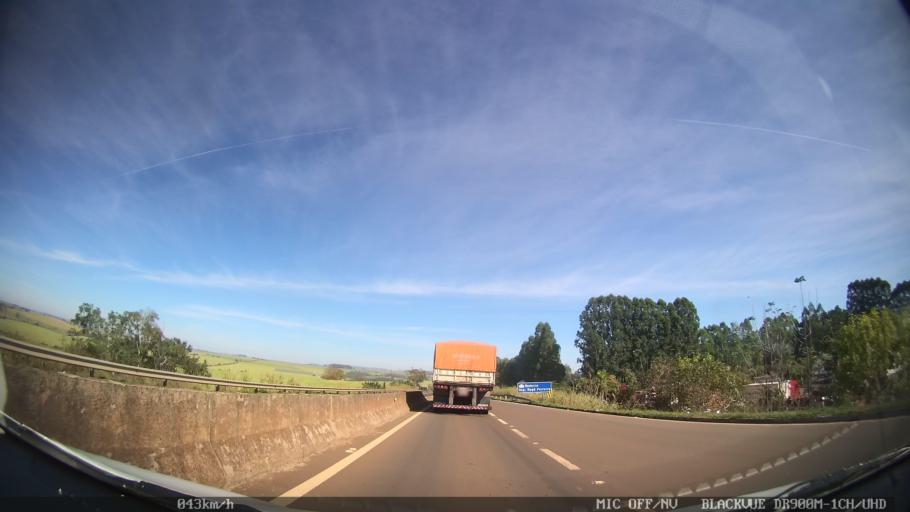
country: BR
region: Sao Paulo
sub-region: Pirassununga
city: Pirassununga
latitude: -22.0393
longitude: -47.4342
